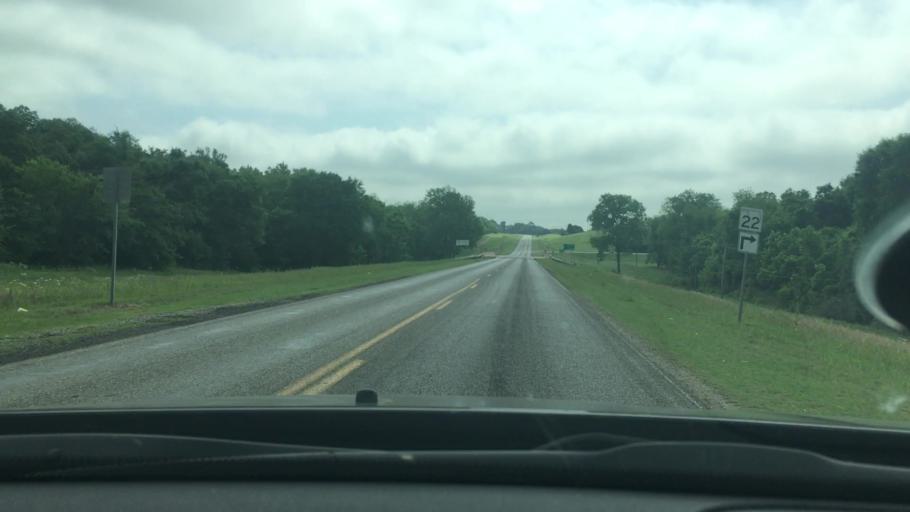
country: US
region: Oklahoma
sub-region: Johnston County
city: Tishomingo
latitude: 34.2303
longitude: -96.6391
